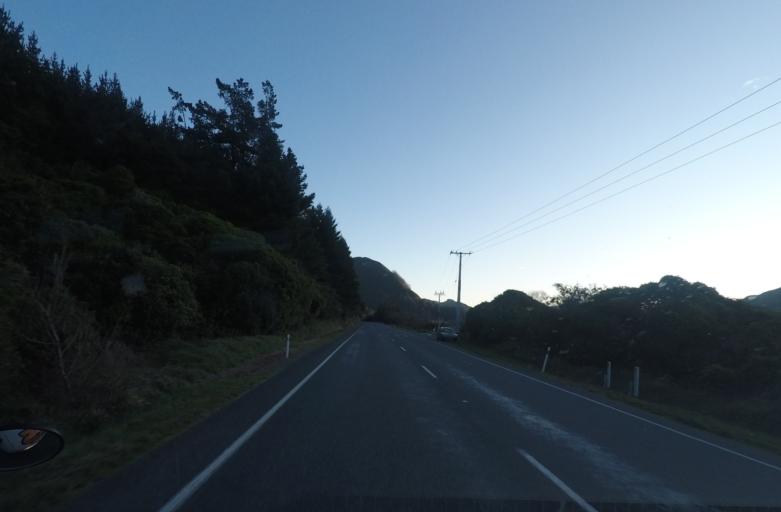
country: NZ
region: Marlborough
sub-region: Marlborough District
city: Picton
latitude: -41.2841
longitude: 173.7145
